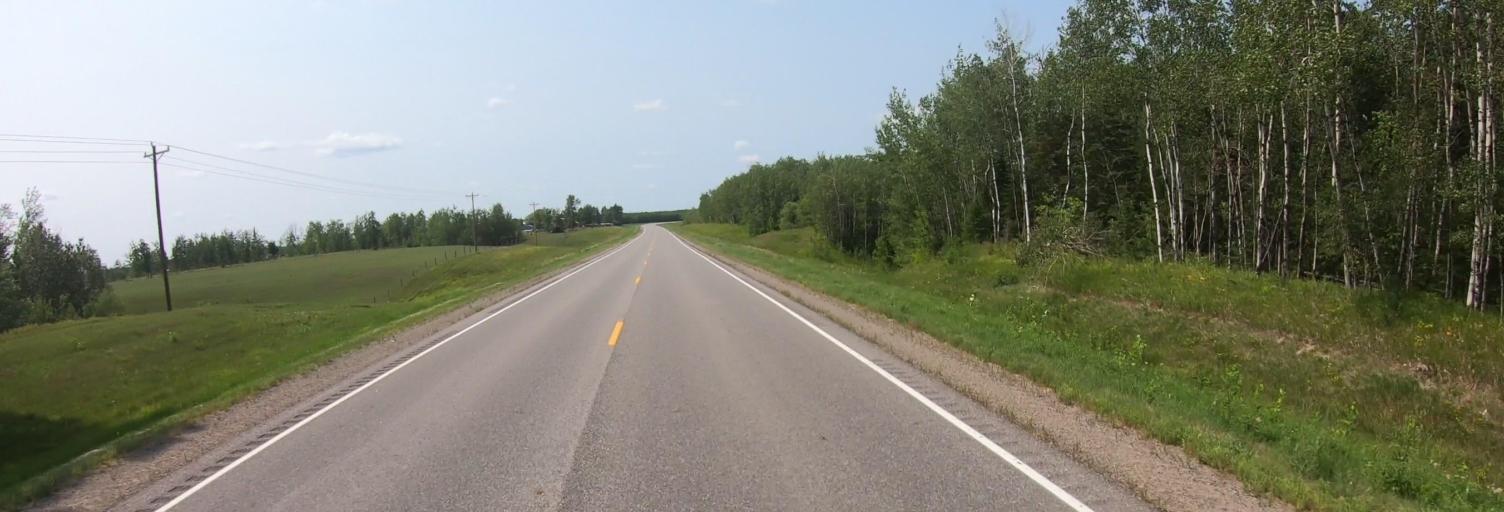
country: US
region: Minnesota
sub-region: Lake of the Woods County
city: Baudette
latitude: 48.6473
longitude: -94.2159
